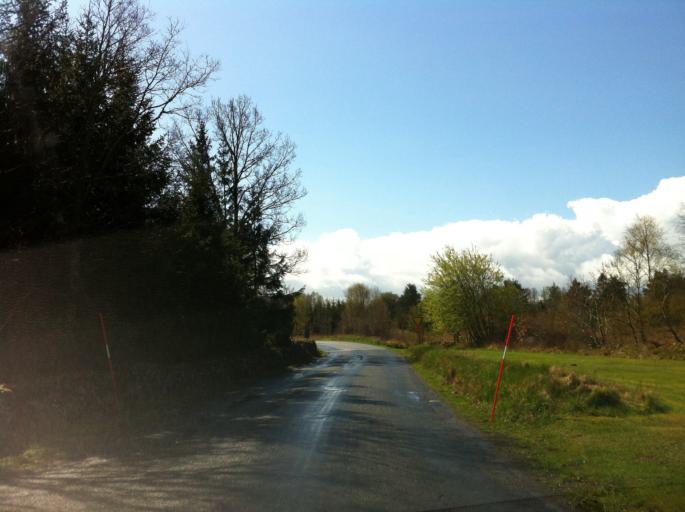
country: SE
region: Skane
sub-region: Hoors Kommun
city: Satofta
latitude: 55.9071
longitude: 13.6098
